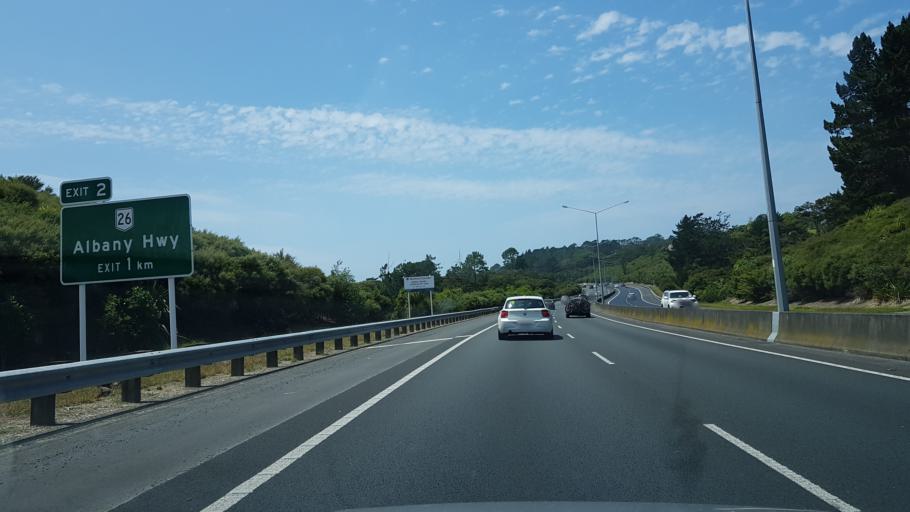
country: NZ
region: Auckland
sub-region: Auckland
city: Rothesay Bay
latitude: -36.7655
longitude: 174.6912
